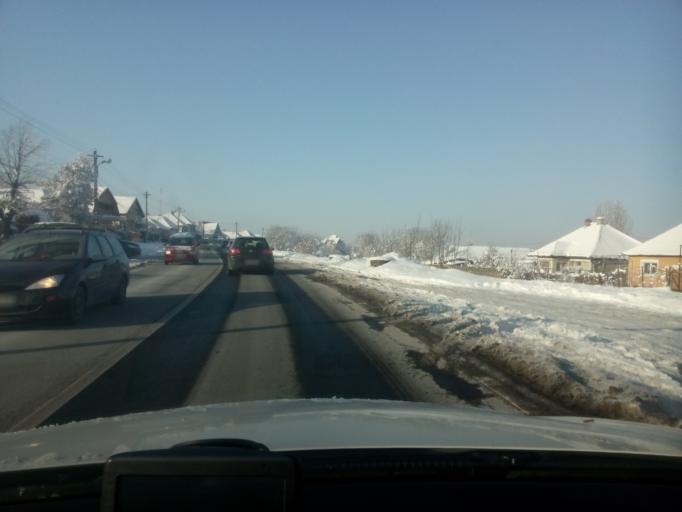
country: RO
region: Sibiu
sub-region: Comuna Talmaciu
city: Talmaciu
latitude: 45.6602
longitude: 24.2638
